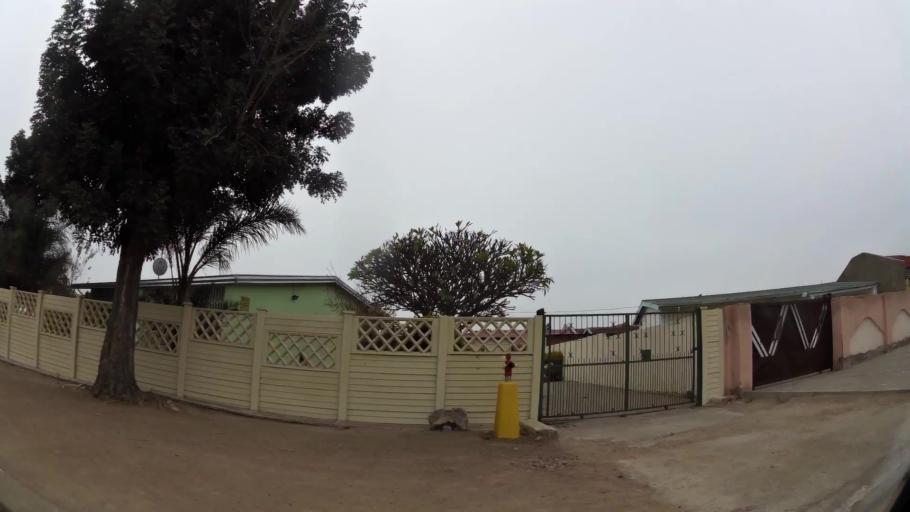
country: ZA
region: Limpopo
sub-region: Capricorn District Municipality
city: Polokwane
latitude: -23.8500
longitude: 29.3922
